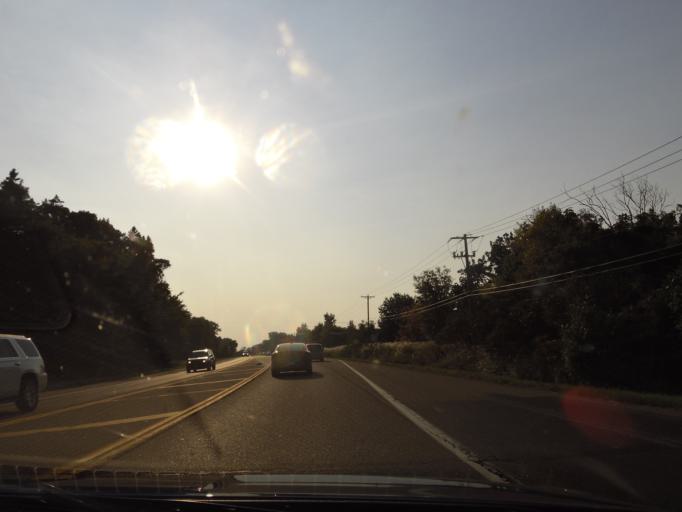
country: US
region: Minnesota
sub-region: Hennepin County
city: Shorewood
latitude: 44.8920
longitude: -93.6013
